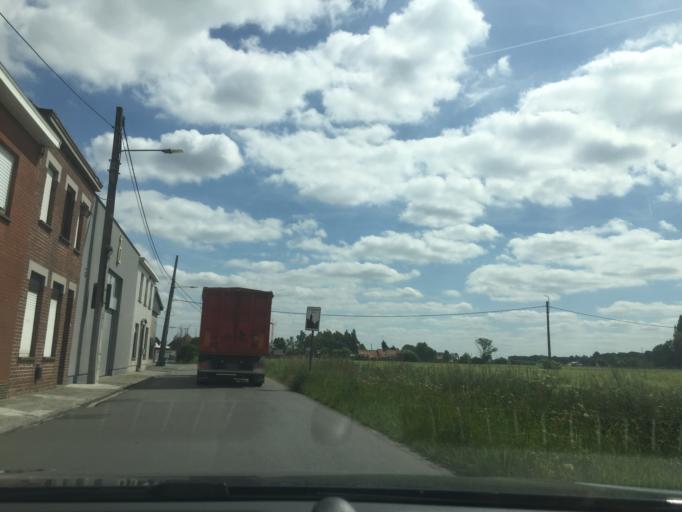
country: BE
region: Flanders
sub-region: Provincie West-Vlaanderen
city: Lendelede
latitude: 50.8715
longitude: 3.2239
